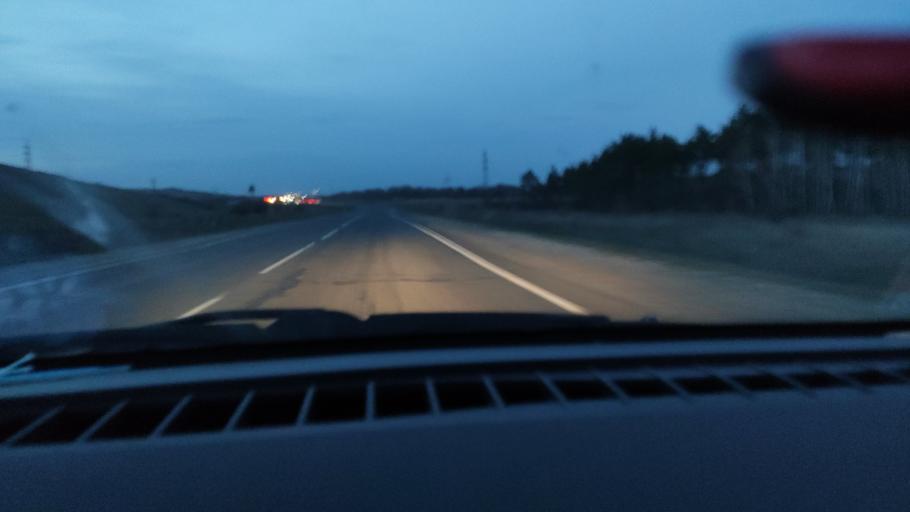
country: RU
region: Saratov
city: Sinodskoye
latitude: 52.0801
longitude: 46.7944
